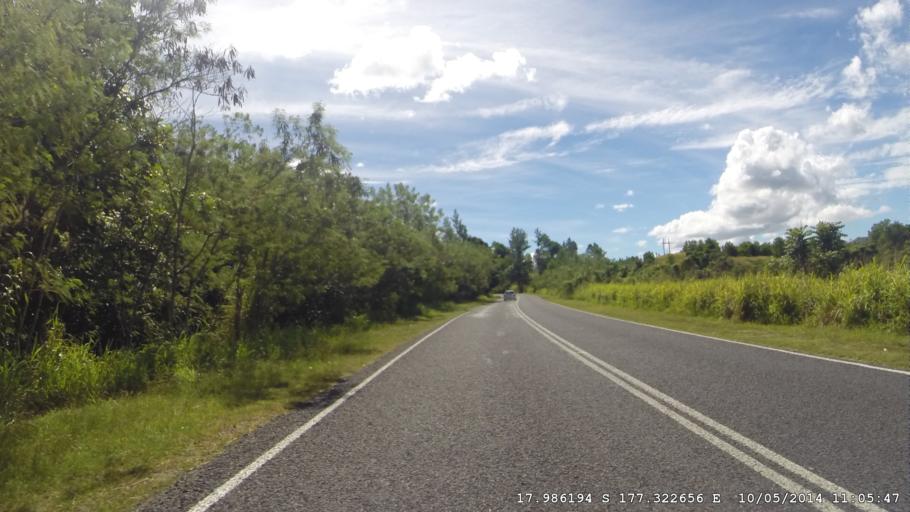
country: FJ
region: Western
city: Nadi
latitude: -17.9862
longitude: 177.3227
